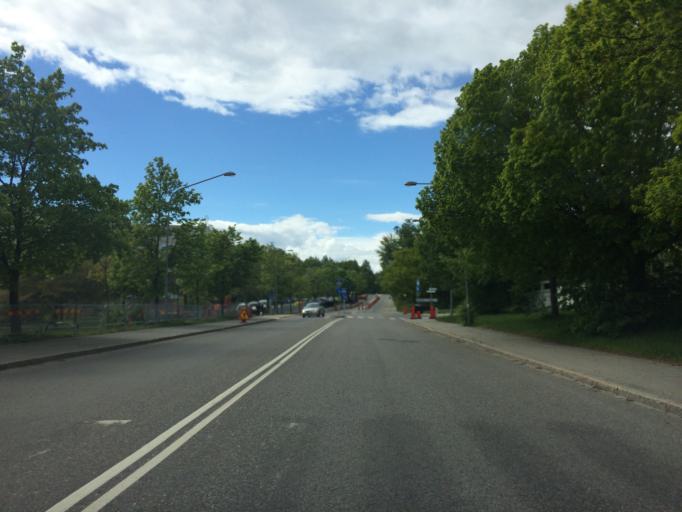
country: SE
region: Stockholm
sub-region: Botkyrka Kommun
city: Fittja
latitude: 59.2722
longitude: 17.8881
